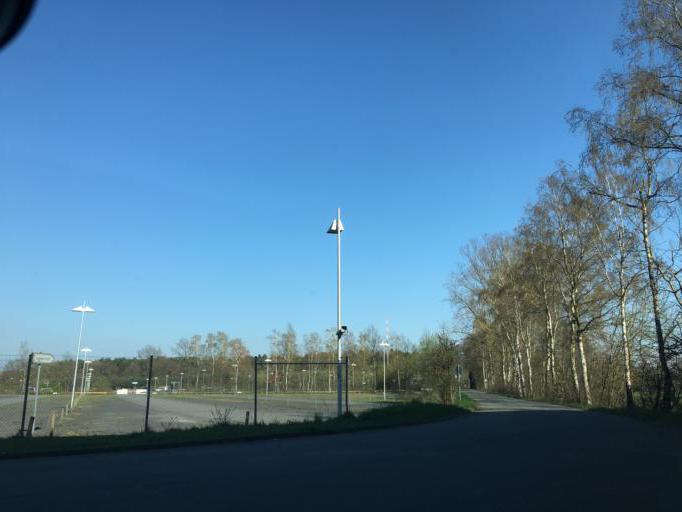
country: DE
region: North Rhine-Westphalia
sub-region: Regierungsbezirk Munster
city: Ladbergen
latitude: 52.1297
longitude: 7.6969
